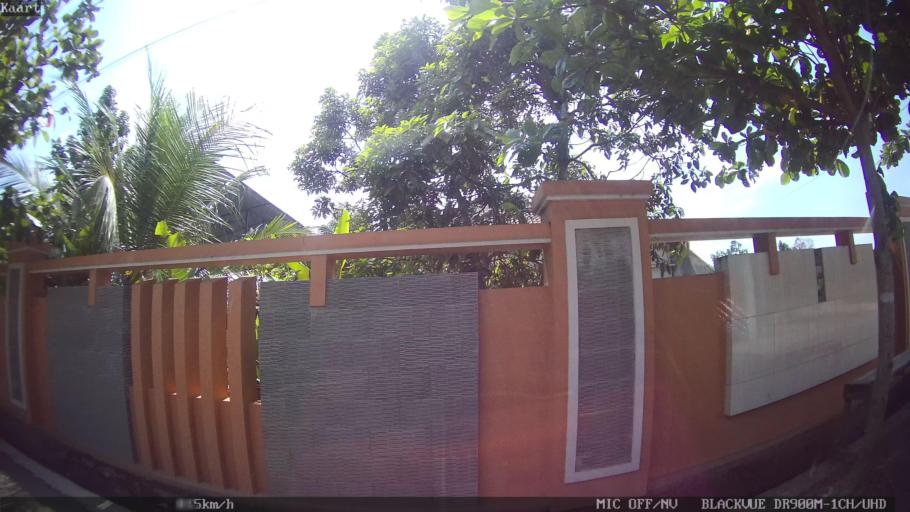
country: ID
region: Lampung
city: Kedaton
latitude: -5.3488
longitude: 105.2764
